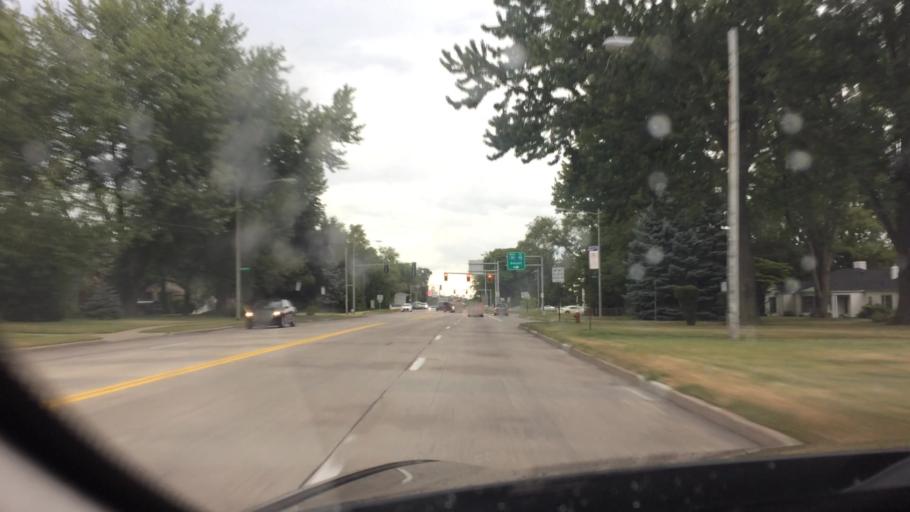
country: US
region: Ohio
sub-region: Lucas County
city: Ottawa Hills
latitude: 41.6863
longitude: -83.6443
